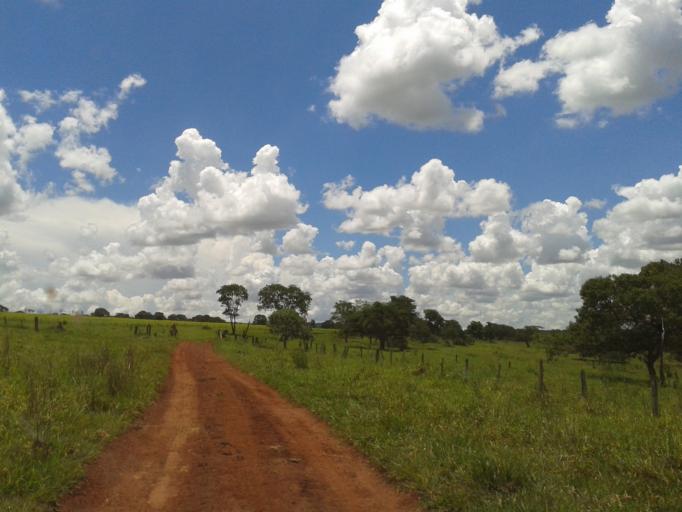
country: BR
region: Minas Gerais
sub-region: Santa Vitoria
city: Santa Vitoria
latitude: -18.7883
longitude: -49.8655
